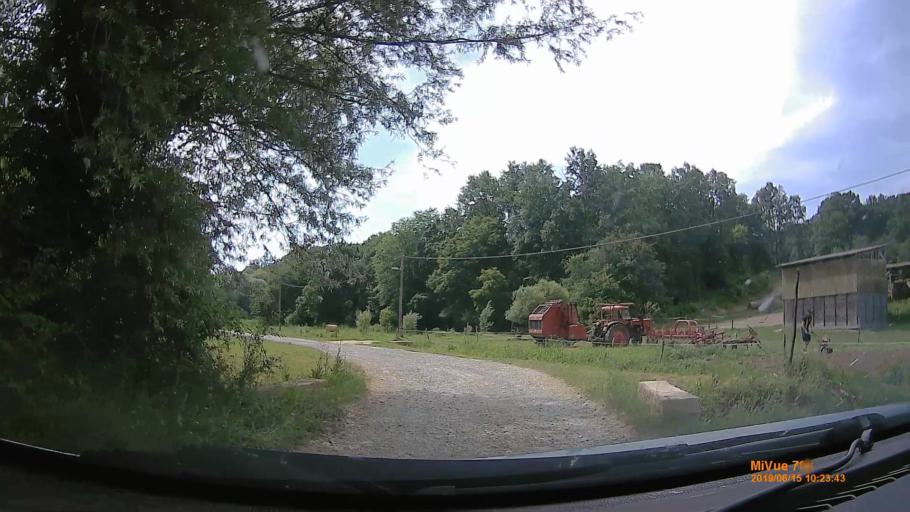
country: HU
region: Baranya
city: Buekkoesd
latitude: 46.1072
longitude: 18.0145
